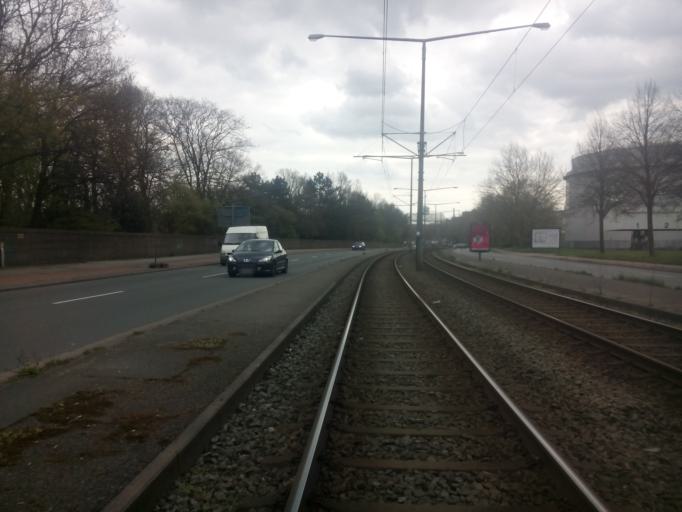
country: DE
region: Bremen
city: Bremen
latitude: 53.1069
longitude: 8.7659
